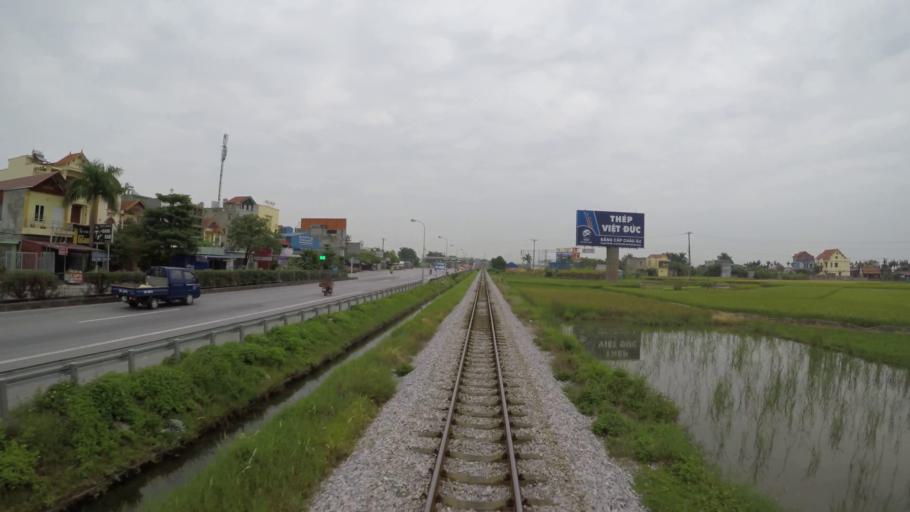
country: VN
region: Hai Duong
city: Phu Thai
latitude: 20.9278
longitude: 106.5557
